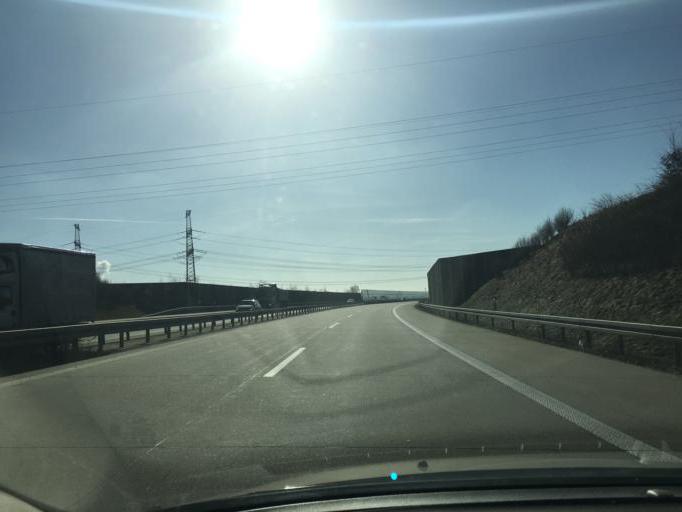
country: DE
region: Saxony
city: Hartmannsdorf
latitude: 50.8662
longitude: 12.8106
